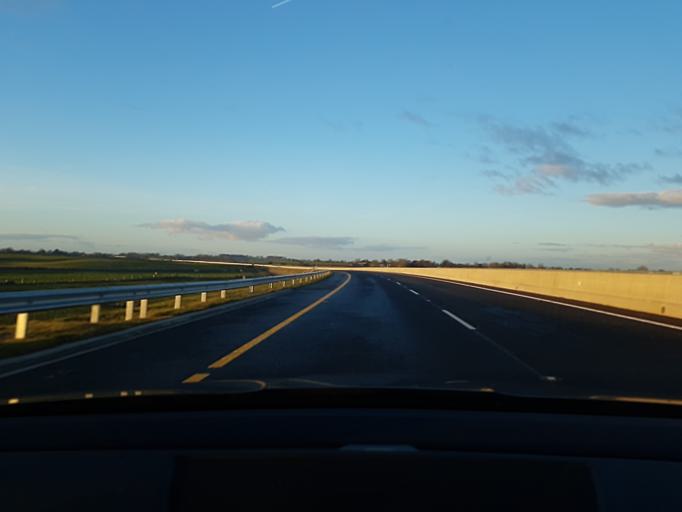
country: IE
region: Connaught
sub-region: County Galway
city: Tuam
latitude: 53.4204
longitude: -8.8298
